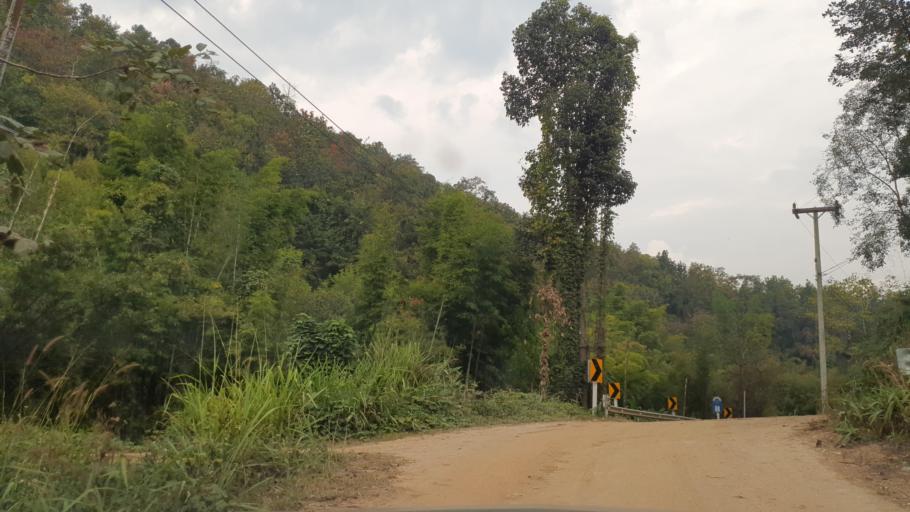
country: TH
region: Chiang Mai
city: Mae Wang
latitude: 18.6556
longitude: 98.6560
